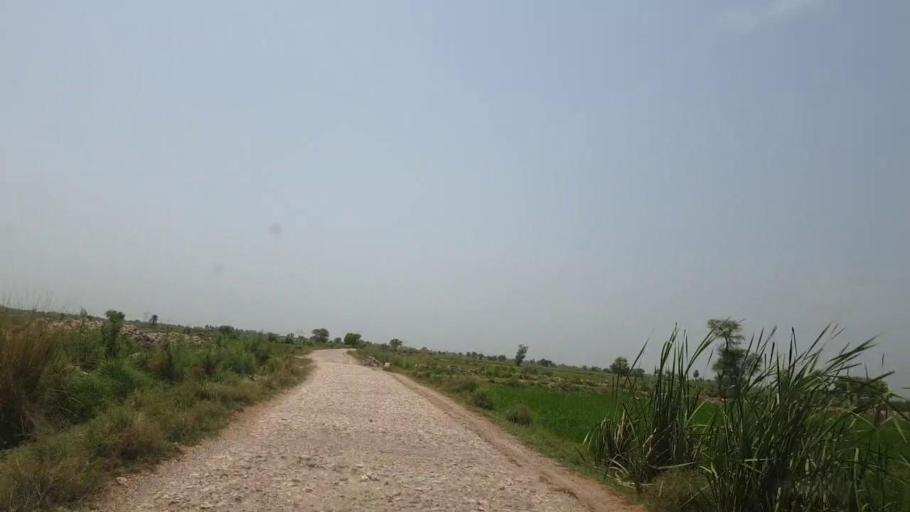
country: PK
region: Sindh
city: Shikarpur
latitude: 27.9056
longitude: 68.6332
